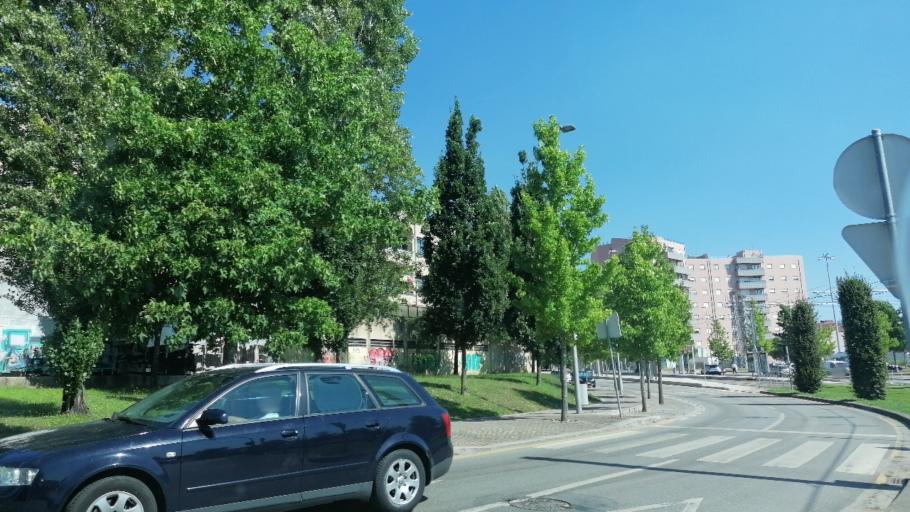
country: PT
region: Porto
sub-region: Gondomar
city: Fanzeres
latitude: 41.1741
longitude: -8.5418
